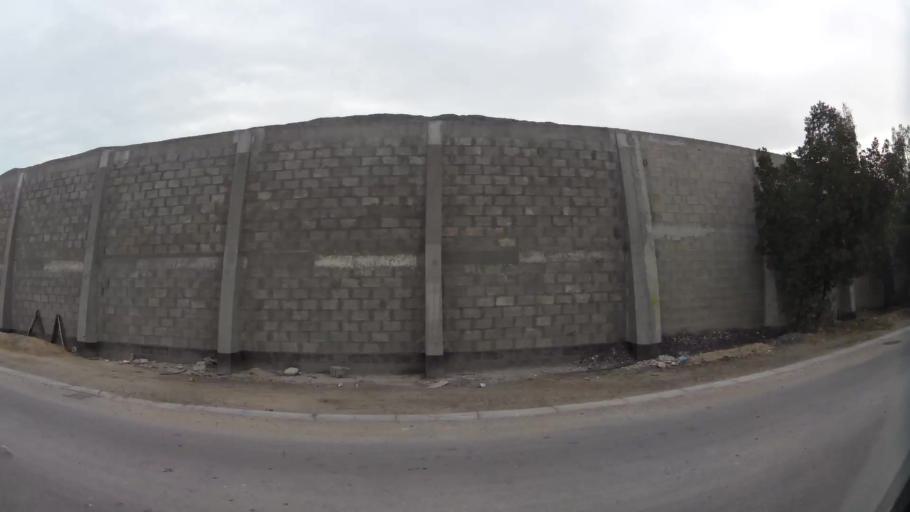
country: BH
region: Northern
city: Sitrah
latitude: 26.1282
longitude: 50.6040
